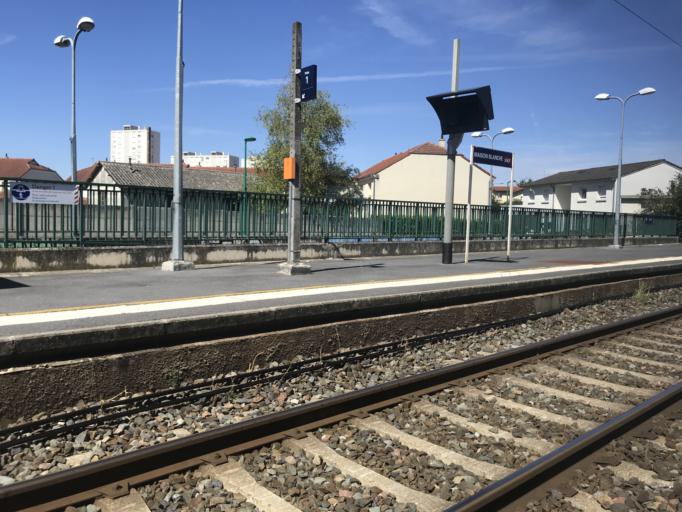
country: FR
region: Champagne-Ardenne
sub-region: Departement de la Marne
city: Reims
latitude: 49.2337
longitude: 4.0225
